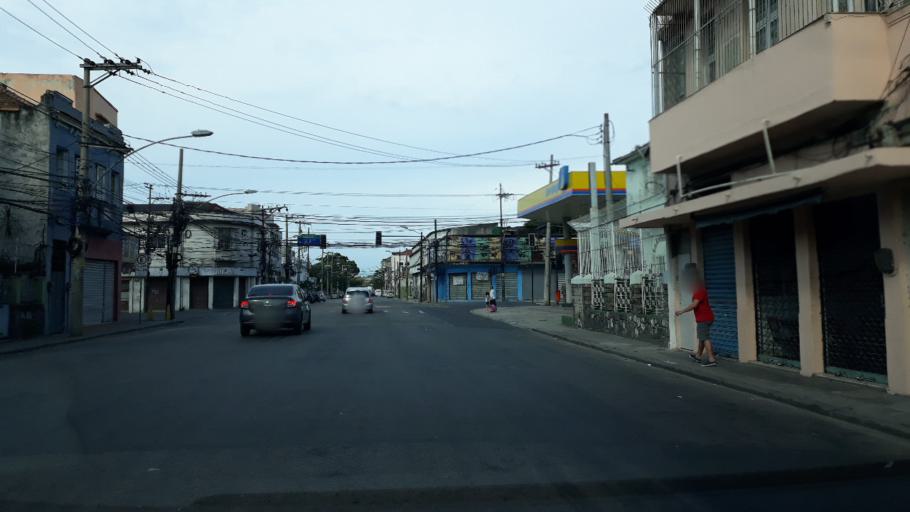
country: BR
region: Rio de Janeiro
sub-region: Rio De Janeiro
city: Rio de Janeiro
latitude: -22.8945
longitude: -43.2395
